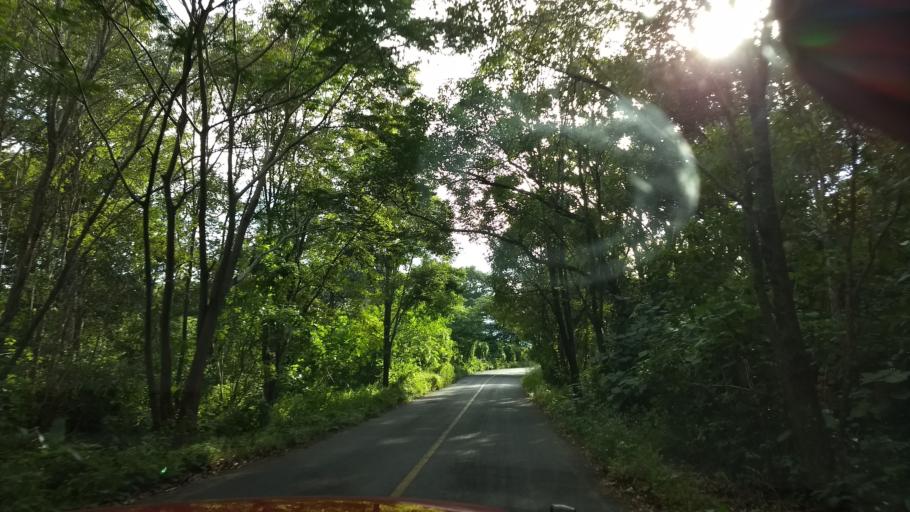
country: MX
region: Colima
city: Suchitlan
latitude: 19.4662
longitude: -103.7715
